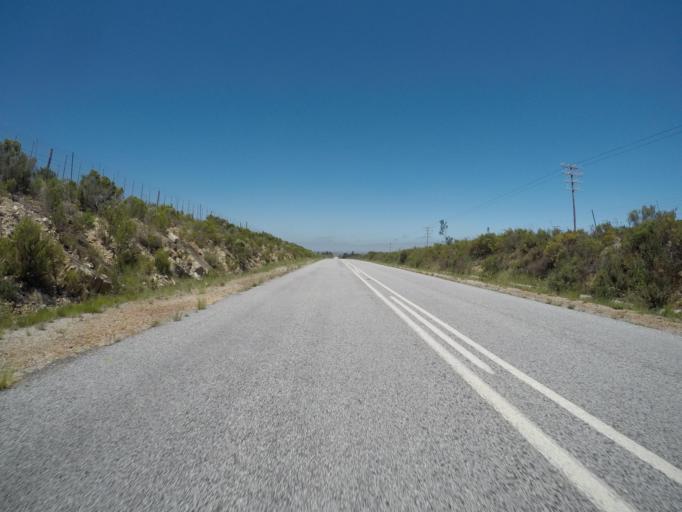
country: ZA
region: Eastern Cape
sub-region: Cacadu District Municipality
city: Kruisfontein
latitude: -33.9910
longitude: 24.5304
